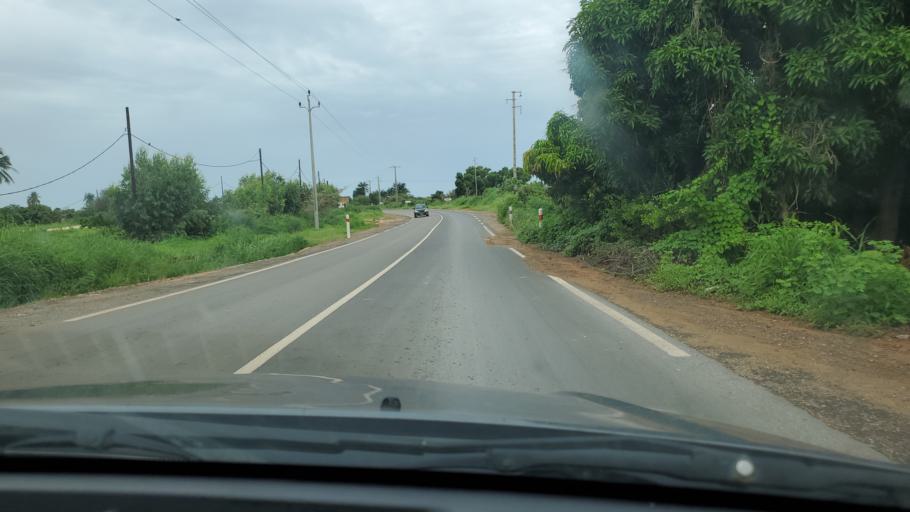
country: SN
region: Thies
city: Mekhe
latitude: 15.1393
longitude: -16.9042
